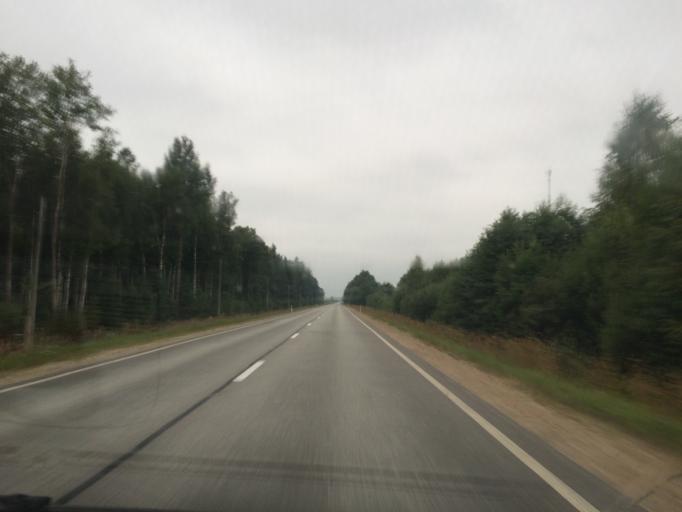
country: LV
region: Varaklani
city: Varaklani
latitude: 56.5236
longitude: 26.4753
